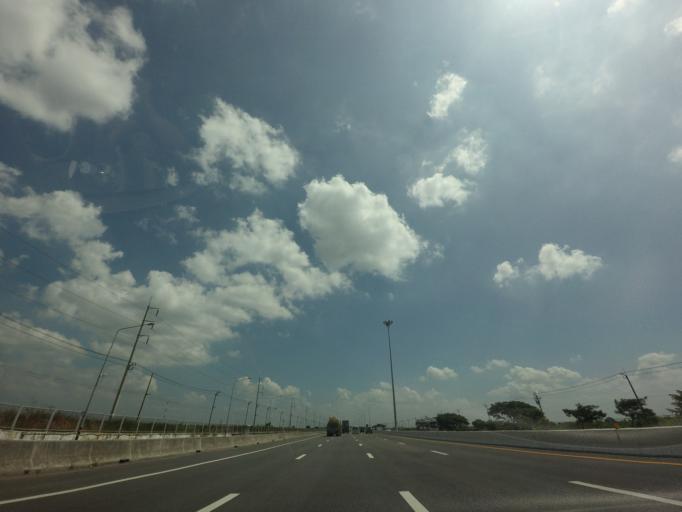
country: TH
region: Samut Prakan
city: Ban Khlong Bang Sao Thong
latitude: 13.6540
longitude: 100.8689
